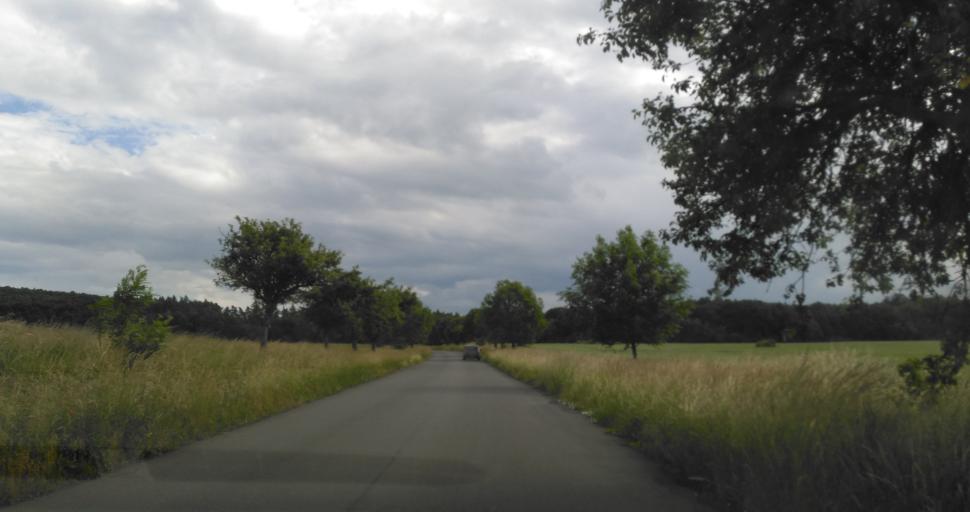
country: CZ
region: Central Bohemia
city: Hostomice
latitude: 49.8760
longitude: 14.0567
